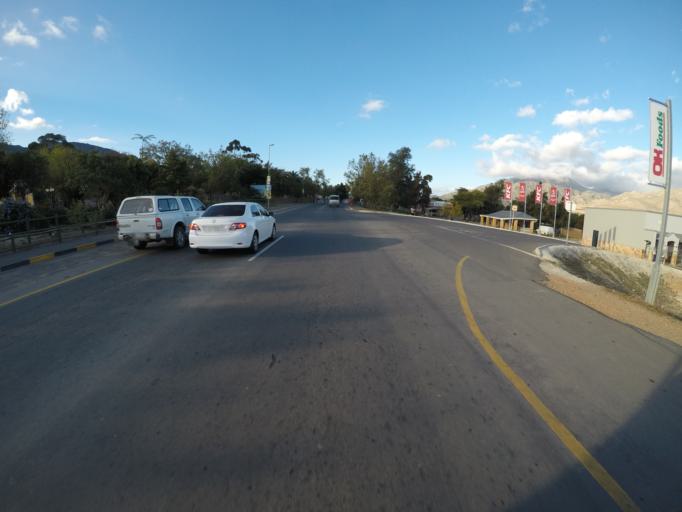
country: ZA
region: Western Cape
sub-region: Overberg District Municipality
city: Caledon
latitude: -33.9939
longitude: 19.2878
